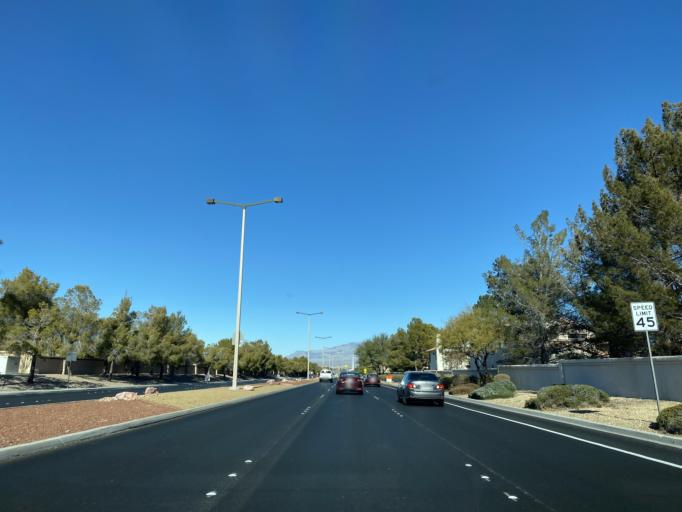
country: US
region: Nevada
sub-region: Clark County
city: Summerlin South
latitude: 36.2108
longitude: -115.2788
